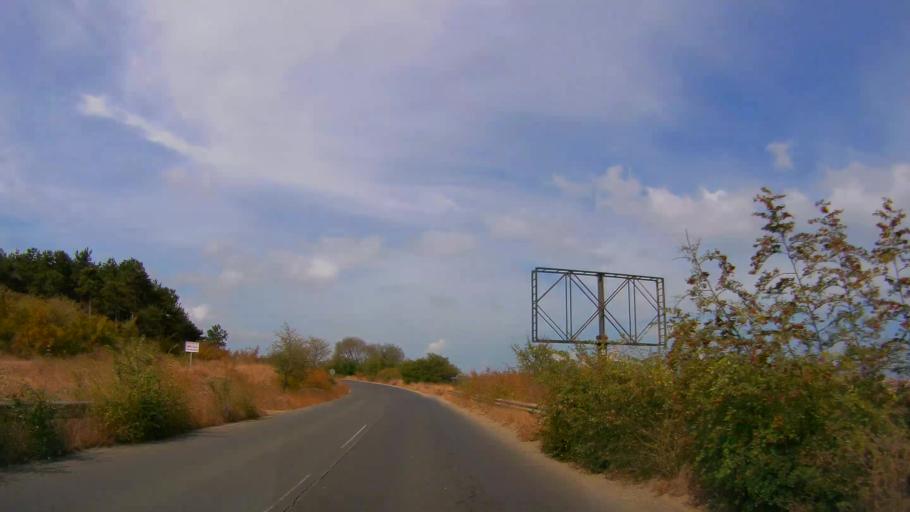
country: BG
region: Burgas
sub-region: Obshtina Sozopol
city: Sozopol
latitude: 42.4091
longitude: 27.6972
